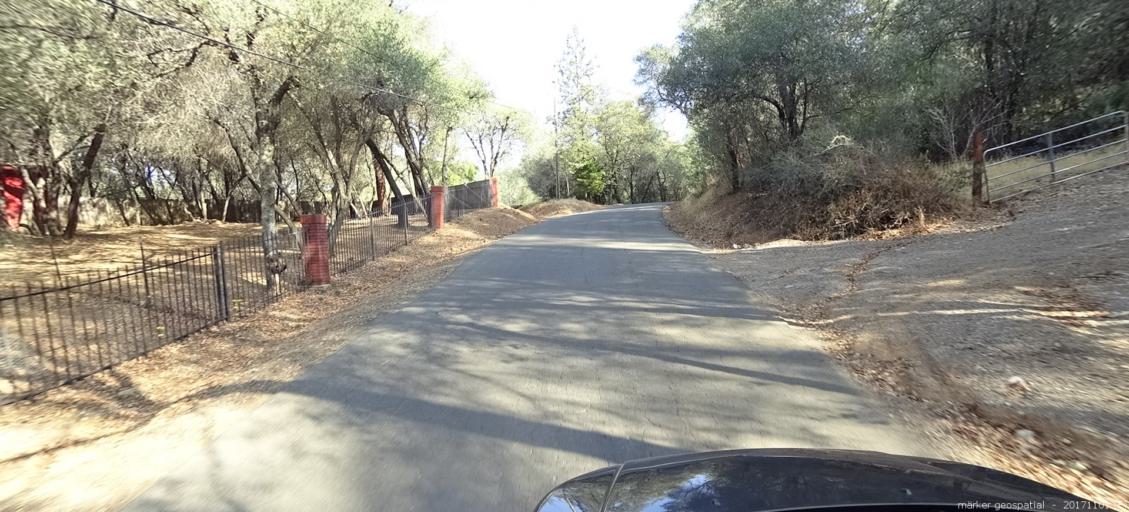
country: US
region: California
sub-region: Shasta County
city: Shasta Lake
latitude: 40.7074
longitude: -122.3266
